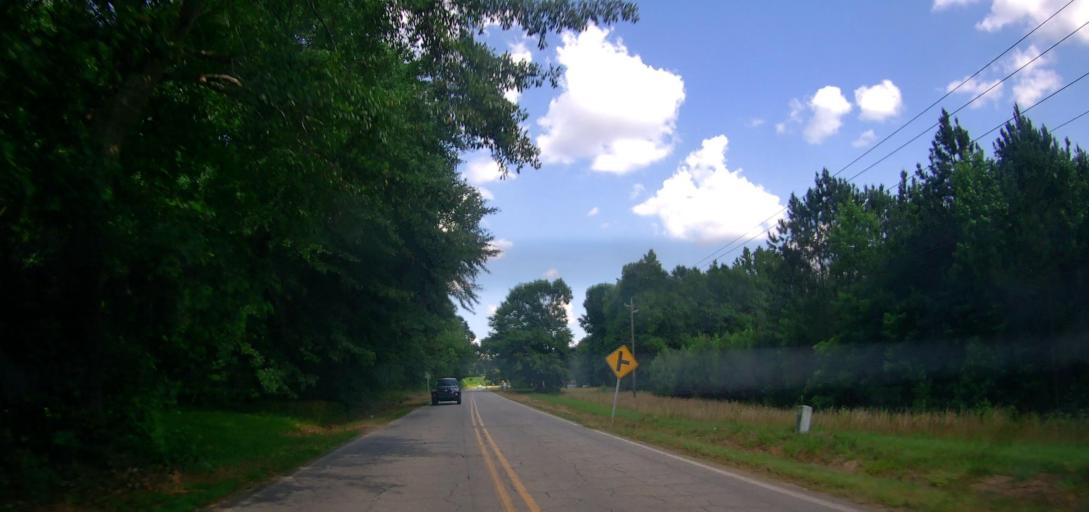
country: US
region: Georgia
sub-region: Spalding County
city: East Griffin
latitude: 33.2351
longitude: -84.1495
